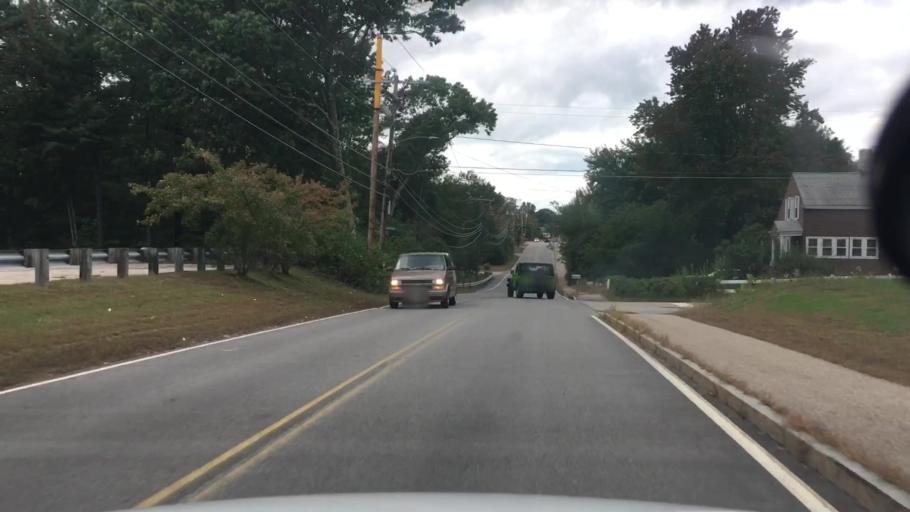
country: US
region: New Hampshire
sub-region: Strafford County
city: Rochester
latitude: 43.2915
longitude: -70.9696
